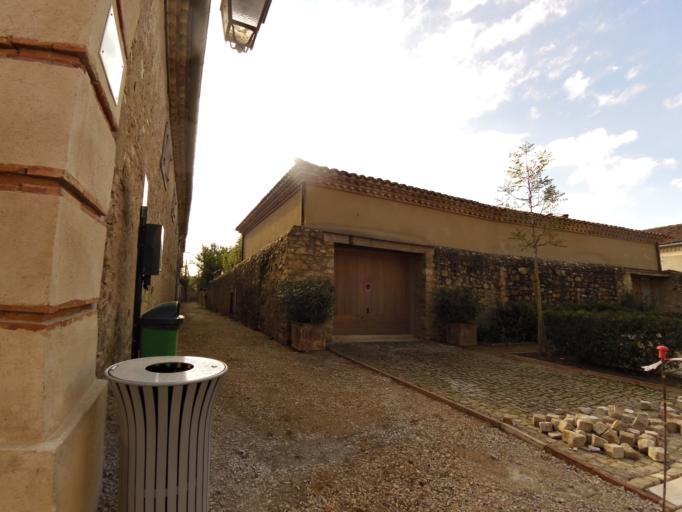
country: FR
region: Midi-Pyrenees
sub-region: Departement du Tarn
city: Soreze
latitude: 43.4512
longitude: 2.0666
